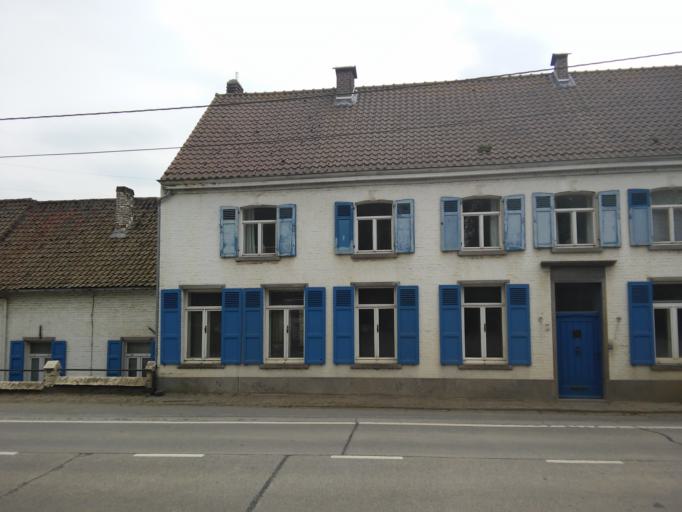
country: BE
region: Flanders
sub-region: Provincie Vlaams-Brabant
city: Halle
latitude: 50.7602
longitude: 4.2171
